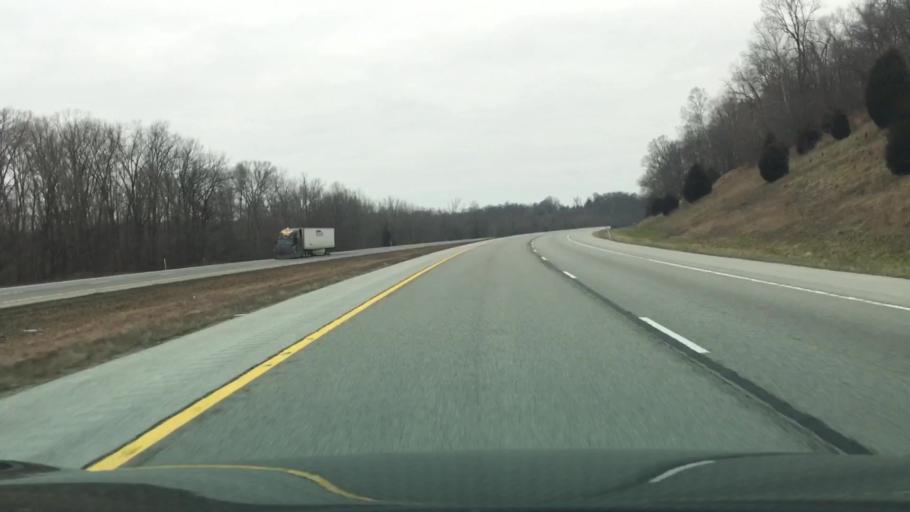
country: US
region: Illinois
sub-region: Johnson County
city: Vienna
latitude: 37.3410
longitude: -88.7860
